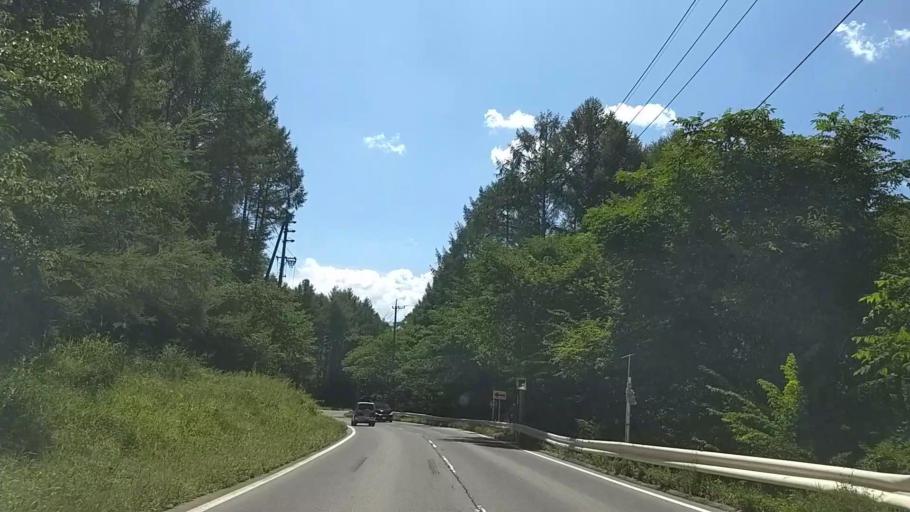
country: JP
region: Nagano
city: Chino
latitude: 36.0686
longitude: 138.2235
